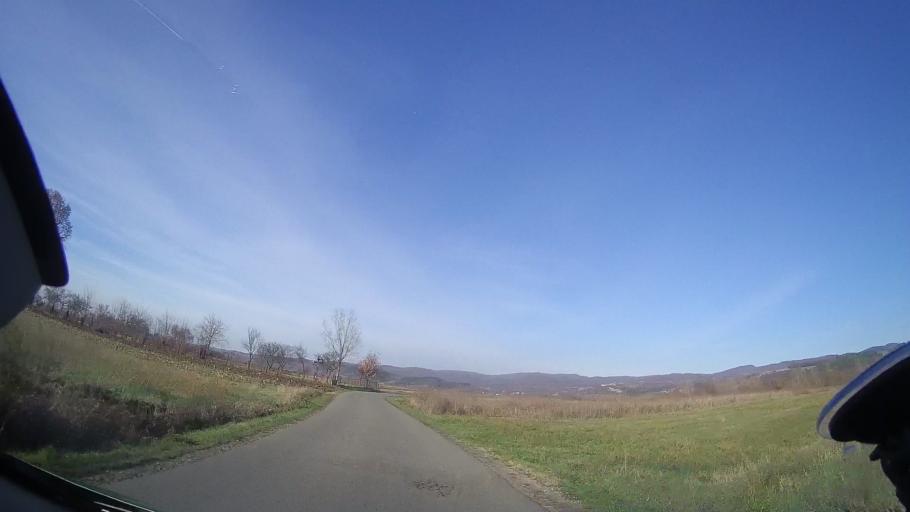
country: RO
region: Bihor
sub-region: Comuna Auseu
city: Auseu
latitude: 47.0257
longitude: 22.4862
